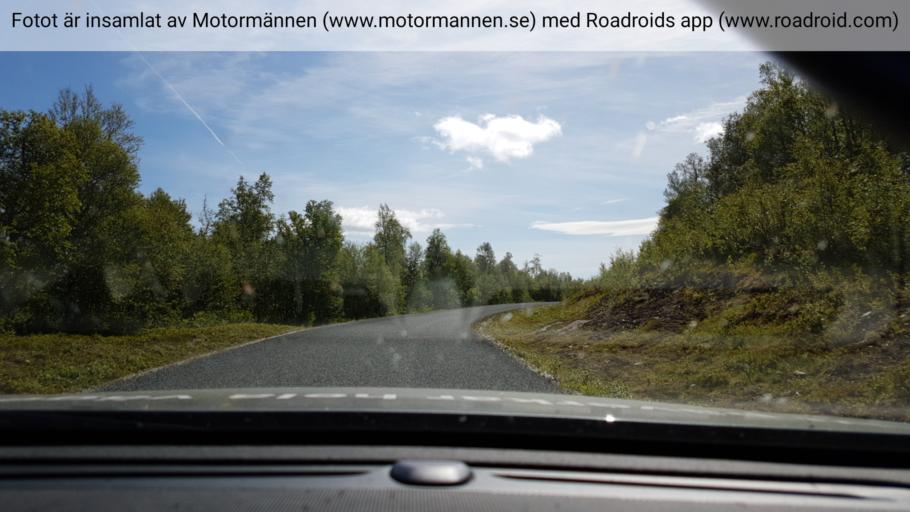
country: NO
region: Nordland
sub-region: Hattfjelldal
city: Hattfjelldal
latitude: 65.4080
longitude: 14.9442
